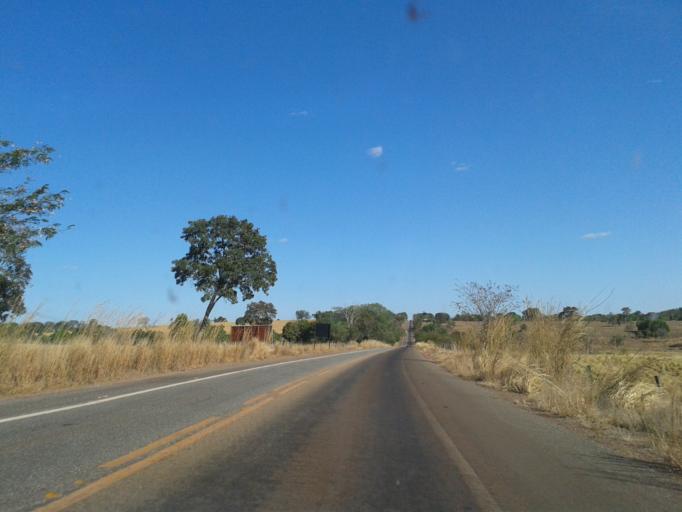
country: BR
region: Goias
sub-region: Mozarlandia
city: Mozarlandia
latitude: -14.7719
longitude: -50.5369
